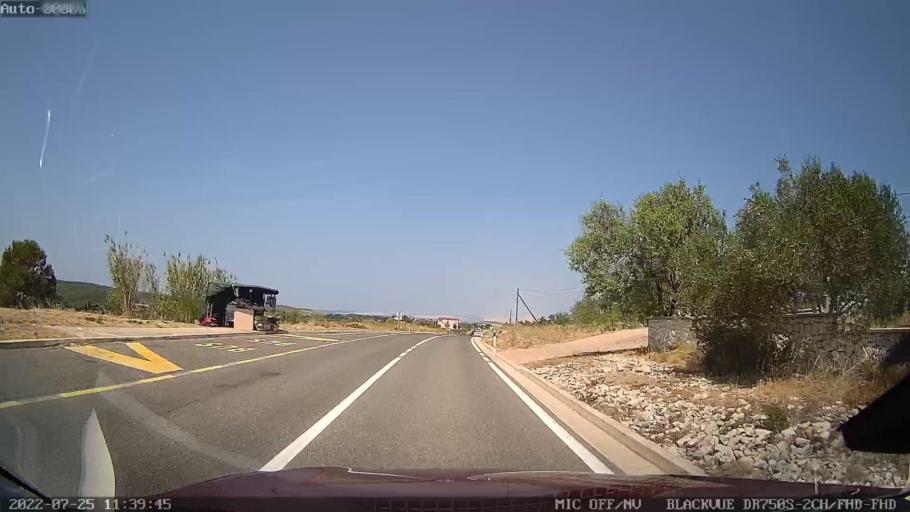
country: HR
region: Zadarska
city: Razanac
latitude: 44.2587
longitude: 15.3684
